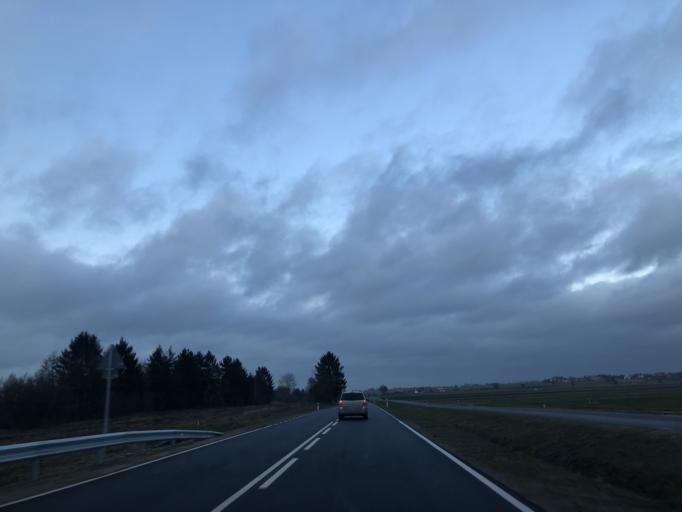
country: PL
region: Podlasie
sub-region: Lomza
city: Lomza
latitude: 53.1302
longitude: 22.0487
